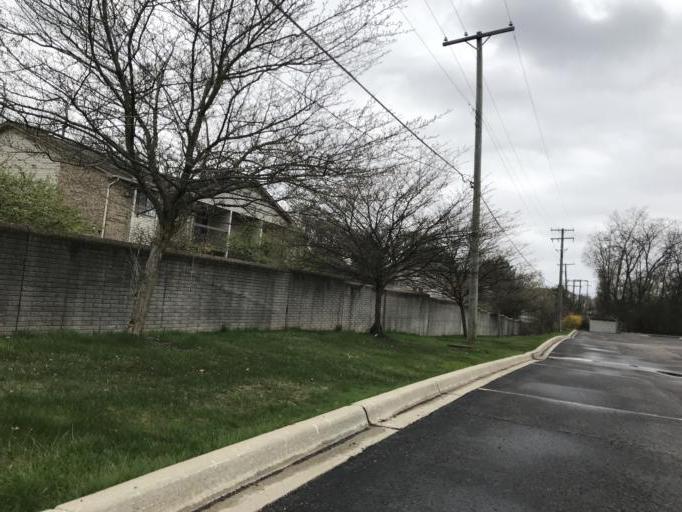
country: US
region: Michigan
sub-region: Oakland County
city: Farmington
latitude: 42.4700
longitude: -83.3354
